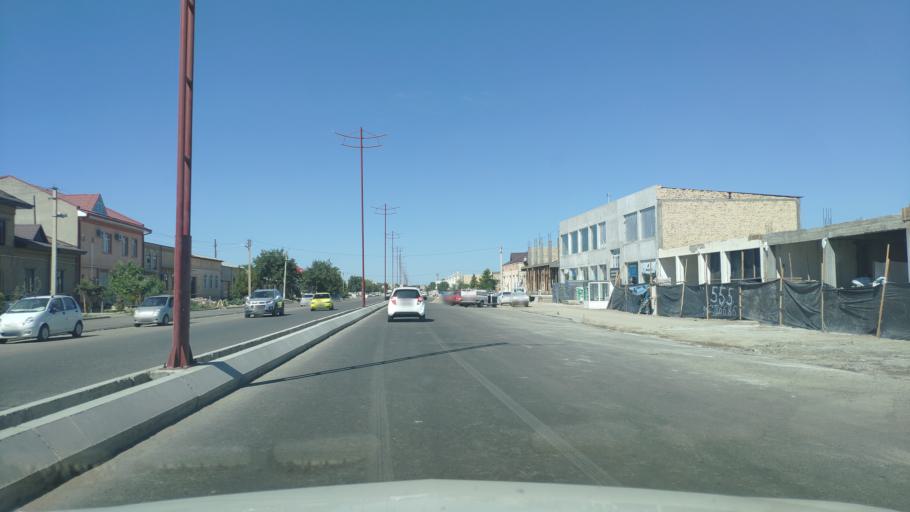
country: UZ
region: Bukhara
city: Bukhara
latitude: 39.7742
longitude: 64.3882
